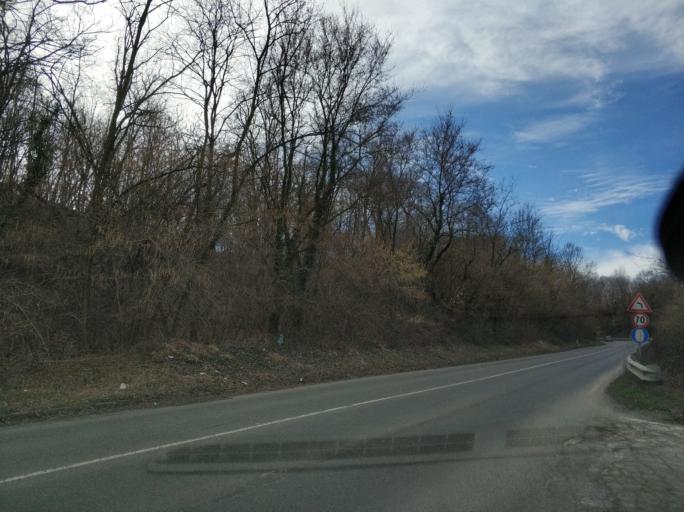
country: IT
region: Piedmont
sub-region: Provincia di Torino
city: Lombardore
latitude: 45.2316
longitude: 7.7342
